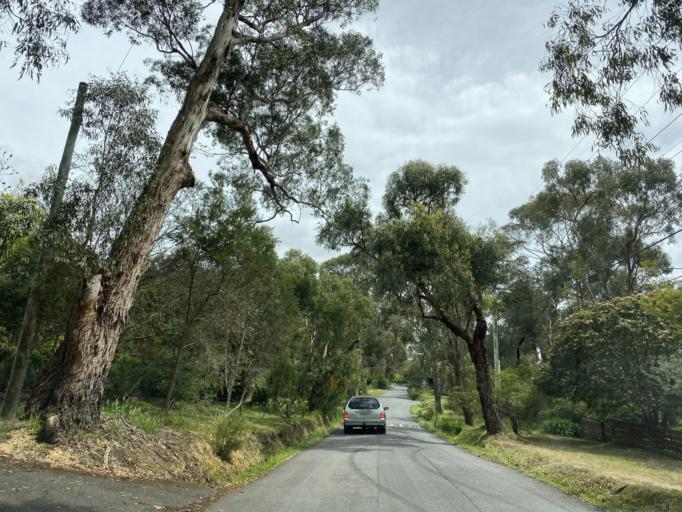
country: AU
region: Victoria
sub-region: Banyule
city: Lower Plenty
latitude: -37.7324
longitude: 145.1262
